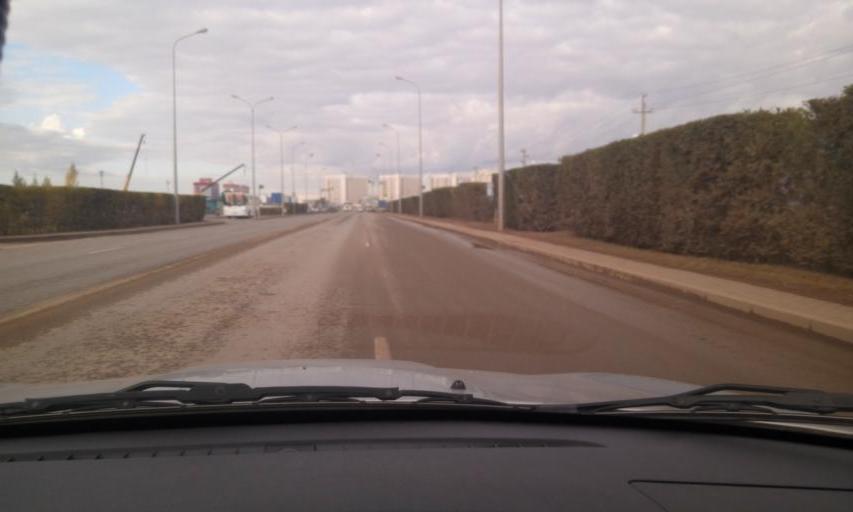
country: KZ
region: Astana Qalasy
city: Astana
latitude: 51.0853
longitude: 71.4099
